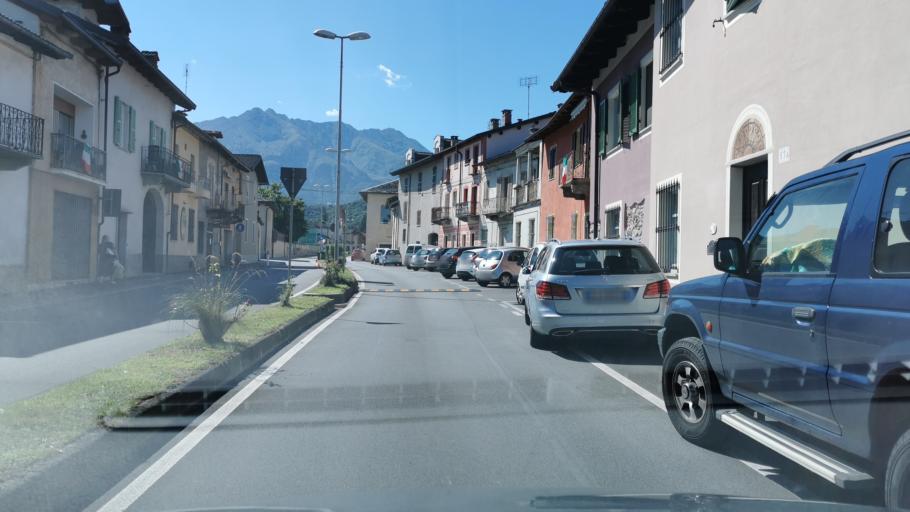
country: IT
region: Piedmont
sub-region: Provincia di Cuneo
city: Boves
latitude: 44.3284
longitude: 7.5486
